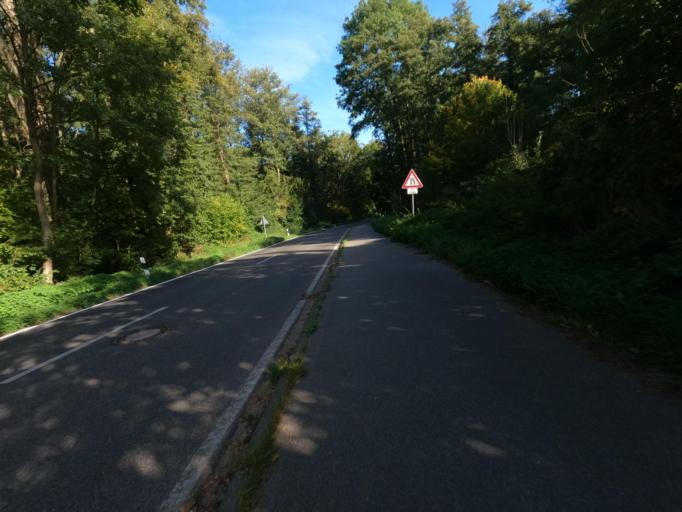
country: DE
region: North Rhine-Westphalia
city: Wegberg
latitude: 51.1727
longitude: 6.2785
